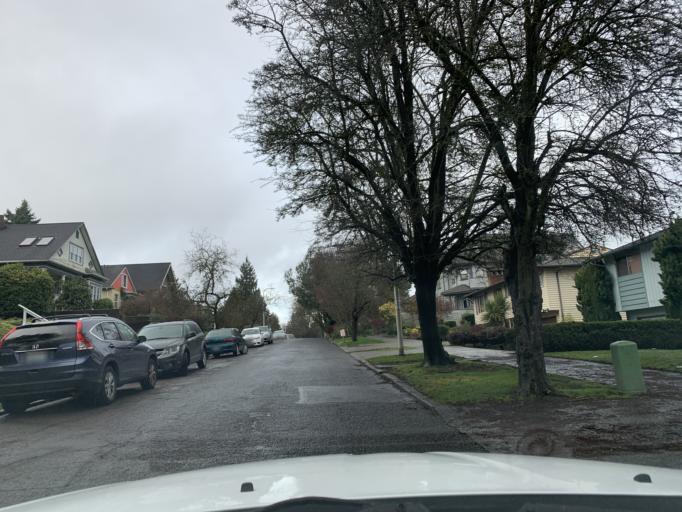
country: US
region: Washington
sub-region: King County
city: Seattle
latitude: 47.6045
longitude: -122.2937
